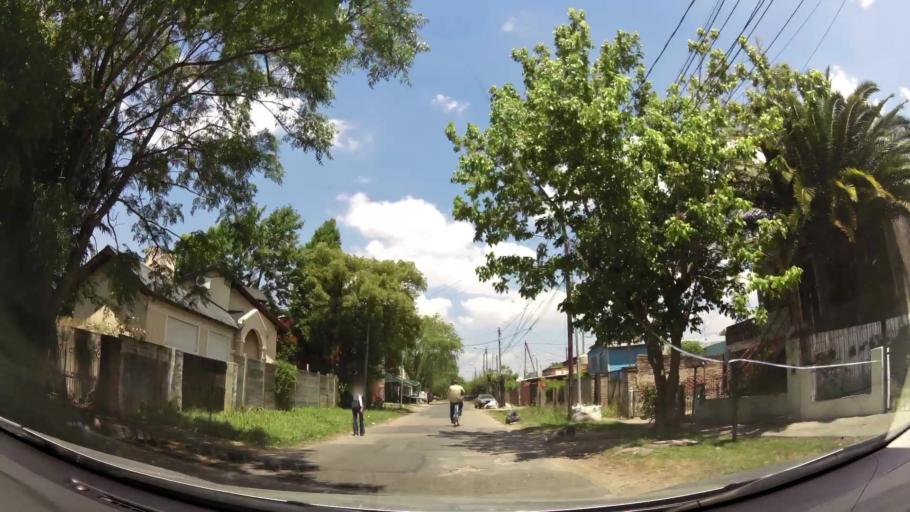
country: AR
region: Buenos Aires
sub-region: Partido de Tigre
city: Tigre
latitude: -34.4128
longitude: -58.5964
